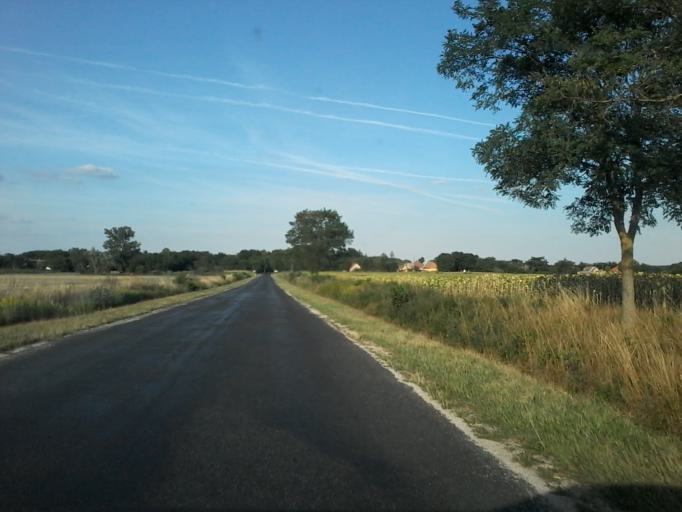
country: HU
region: Vas
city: Celldomolk
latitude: 47.2072
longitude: 17.0991
